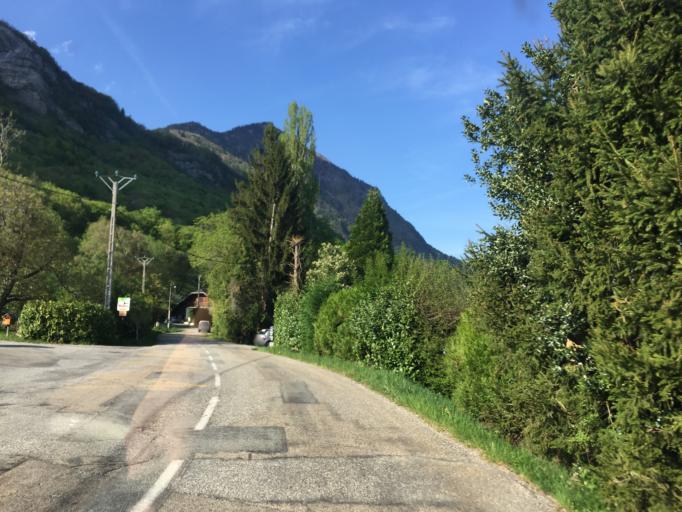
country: FR
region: Rhone-Alpes
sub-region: Departement de la Savoie
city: Mercury
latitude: 45.6660
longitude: 6.3194
